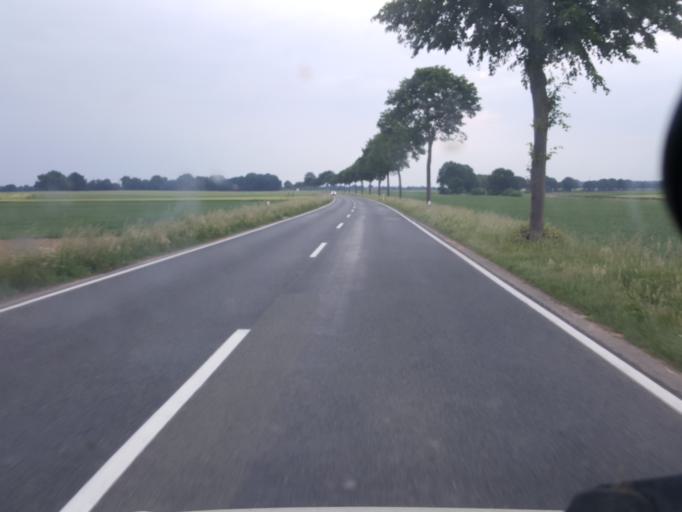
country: DE
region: Lower Saxony
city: Stolzenau
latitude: 52.5019
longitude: 9.0508
